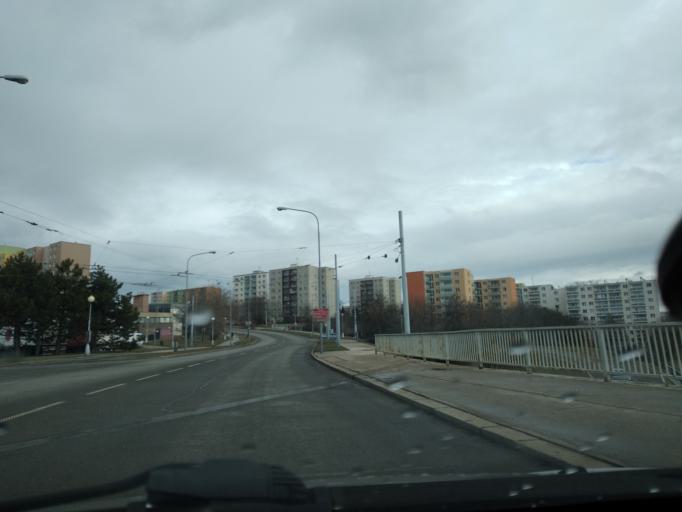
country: CZ
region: South Moravian
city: Ostopovice
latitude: 49.1691
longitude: 16.5668
